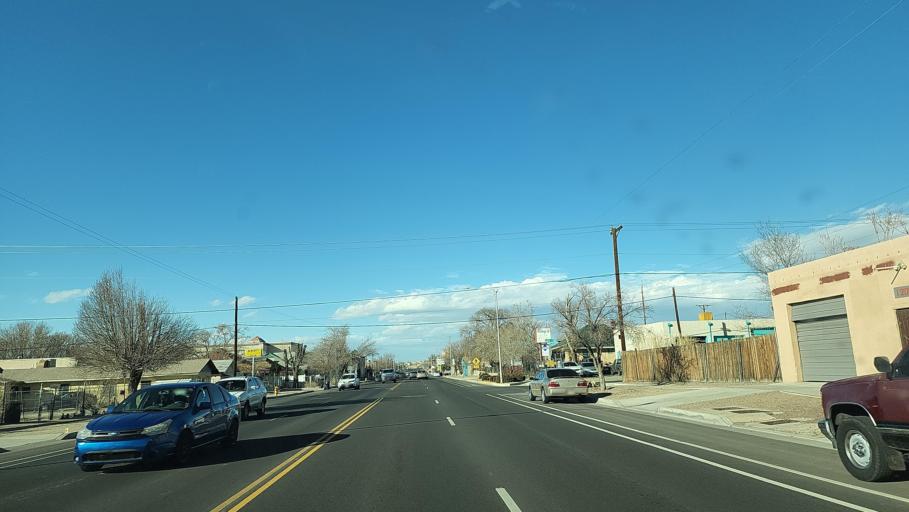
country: US
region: New Mexico
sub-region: Bernalillo County
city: Albuquerque
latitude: 35.0712
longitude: -106.6456
